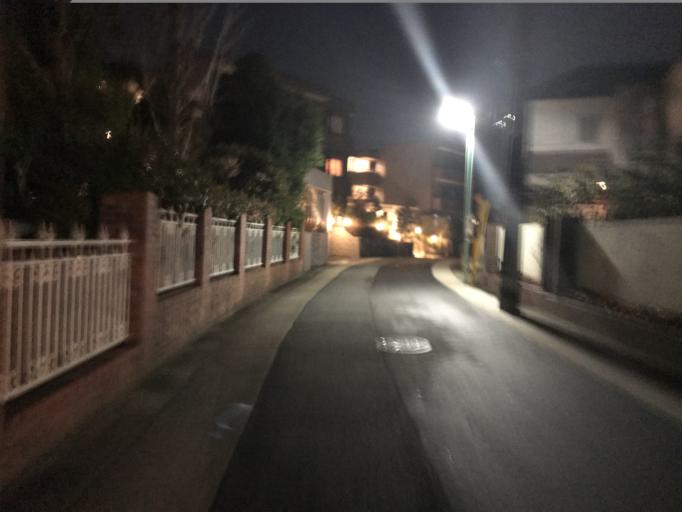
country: JP
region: Aichi
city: Nagoya-shi
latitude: 35.1343
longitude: 136.9686
